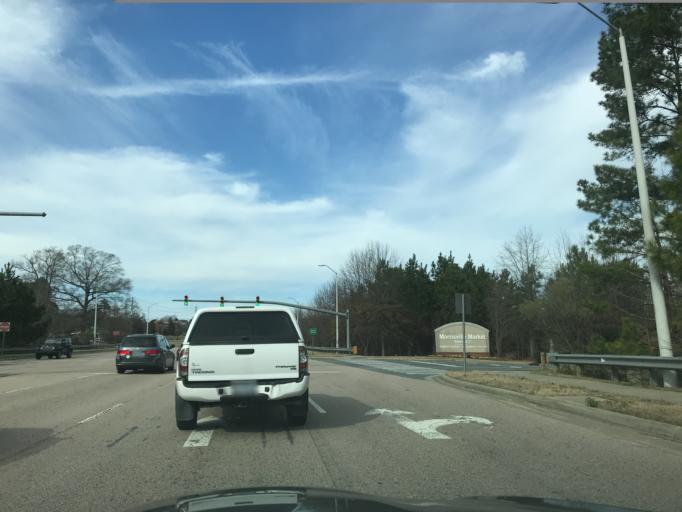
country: US
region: North Carolina
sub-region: Wake County
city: Morrisville
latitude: 35.8168
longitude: -78.8473
